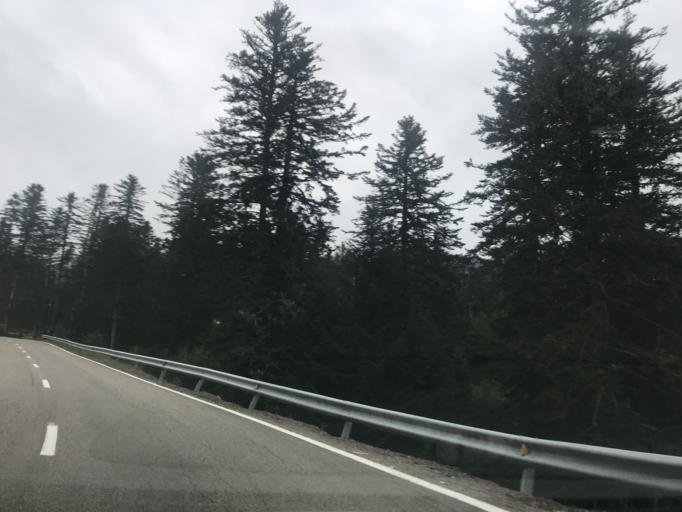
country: ES
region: Catalonia
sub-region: Provincia de Lleida
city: Les
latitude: 42.7665
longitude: 0.6630
